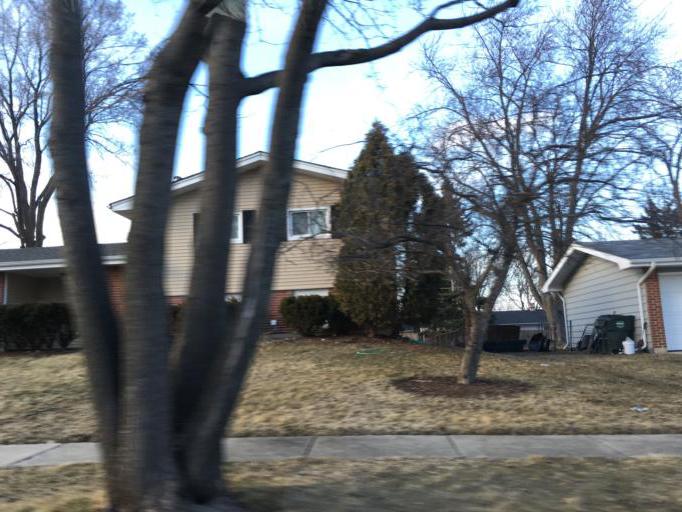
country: US
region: Illinois
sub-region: Cook County
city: Schaumburg
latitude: 42.0436
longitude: -88.0969
